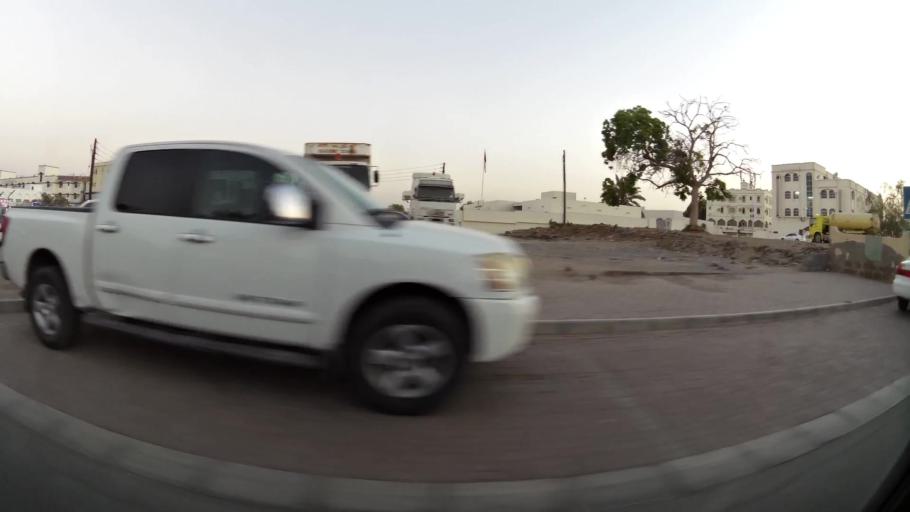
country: OM
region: Muhafazat Masqat
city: As Sib al Jadidah
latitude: 23.6840
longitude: 58.1825
